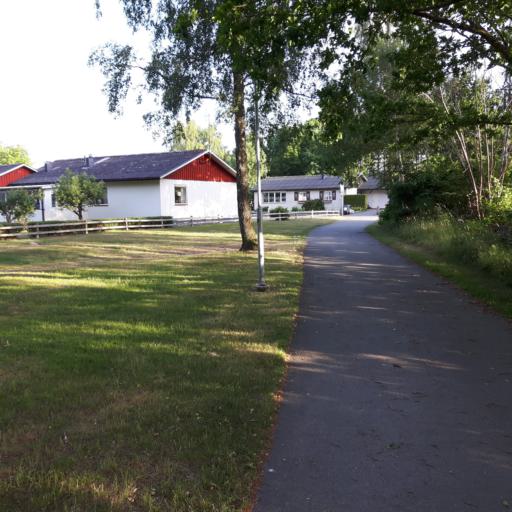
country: SE
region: Skane
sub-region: Hassleholms Kommun
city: Vinslov
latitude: 56.0973
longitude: 13.9063
